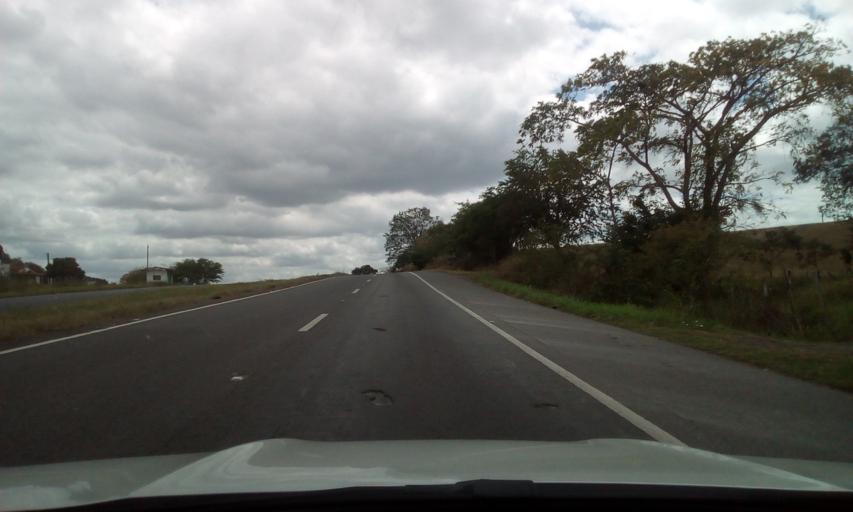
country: BR
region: Paraiba
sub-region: Fagundes
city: Fagundes
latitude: -7.2748
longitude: -35.7270
